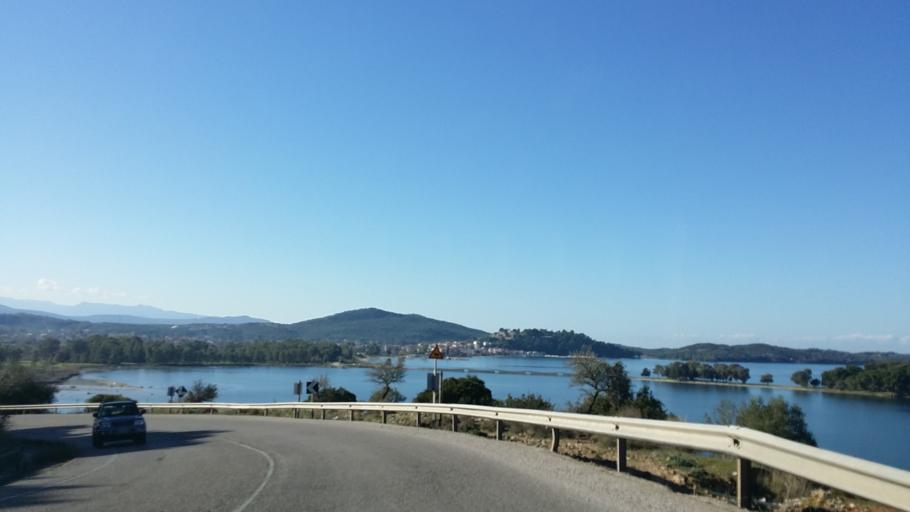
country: GR
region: West Greece
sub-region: Nomos Aitolias kai Akarnanias
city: Vonitsa
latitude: 38.9250
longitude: 20.9093
